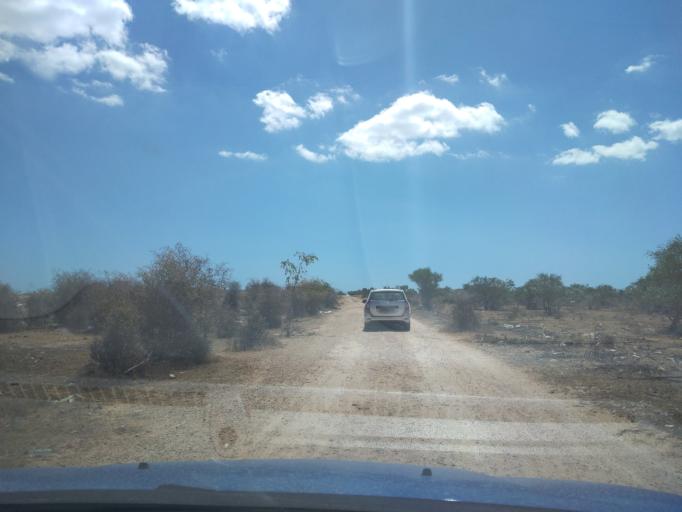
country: TN
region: Susah
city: Harqalah
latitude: 36.1665
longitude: 10.4413
